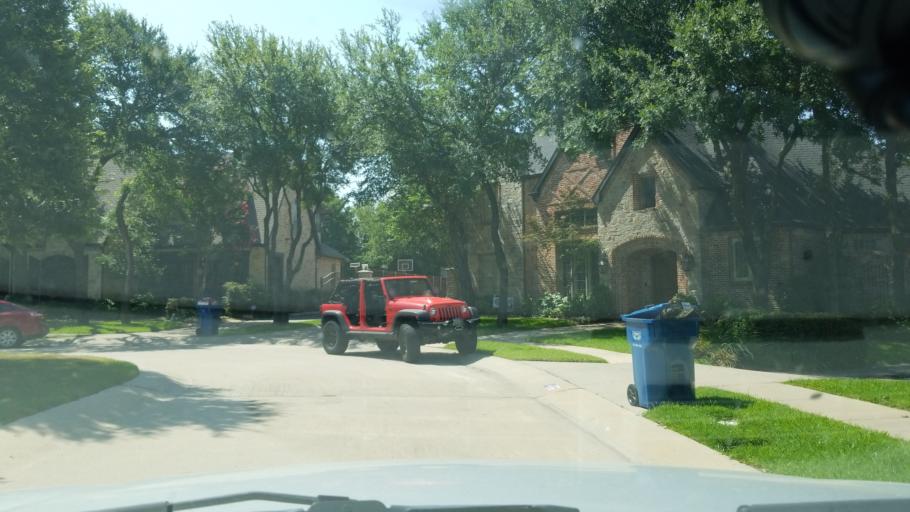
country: US
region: Texas
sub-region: Dallas County
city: Coppell
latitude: 32.9508
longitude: -96.9991
